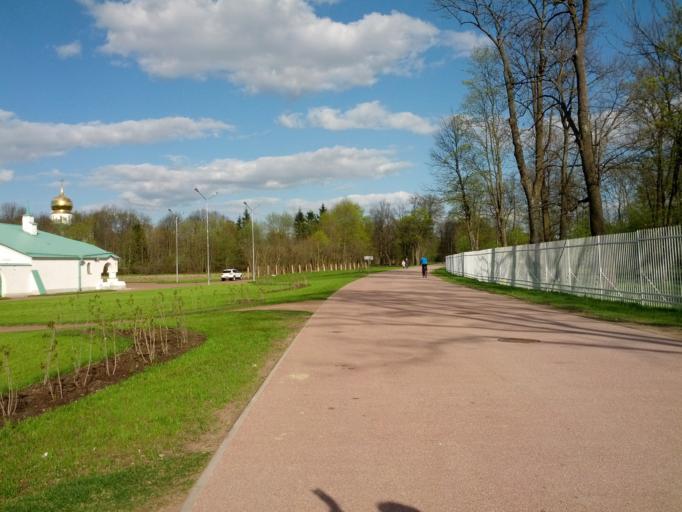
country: RU
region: St.-Petersburg
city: Pushkin
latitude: 59.7250
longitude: 30.3853
